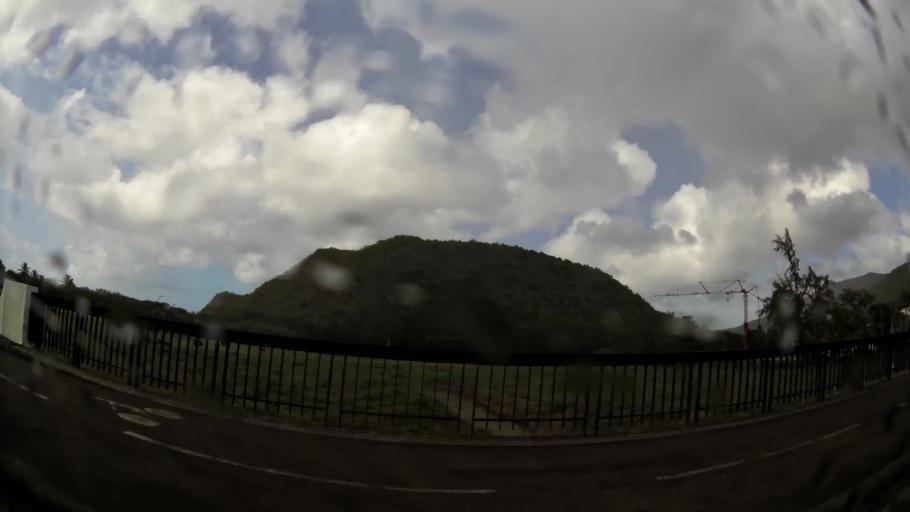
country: MQ
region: Martinique
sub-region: Martinique
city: Les Trois-Ilets
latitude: 14.4946
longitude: -61.0773
